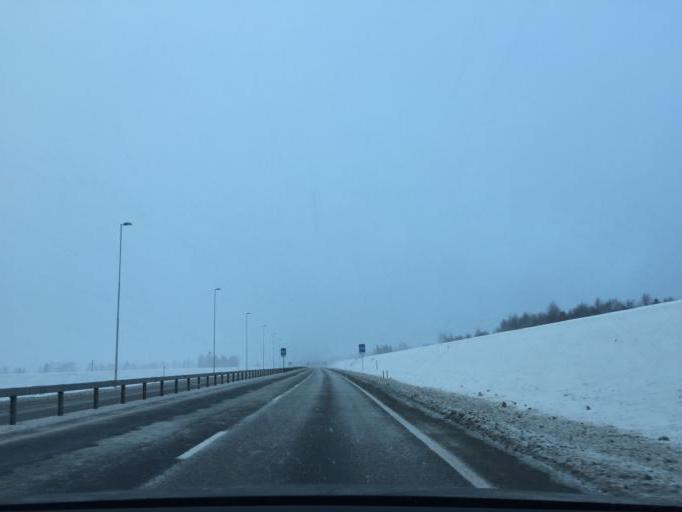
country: NO
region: Hedmark
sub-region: Sor-Odal
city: Skarnes
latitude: 60.2461
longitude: 11.7593
